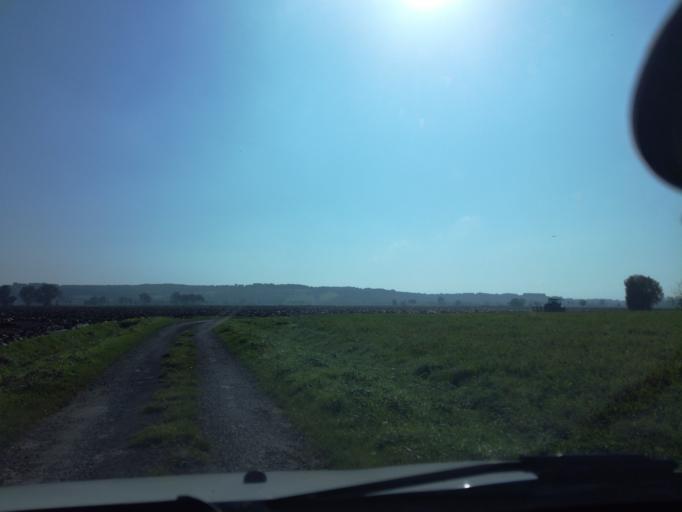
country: FR
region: Brittany
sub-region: Departement d'Ille-et-Vilaine
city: Saint-Broladre
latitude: 48.5943
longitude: -1.6813
